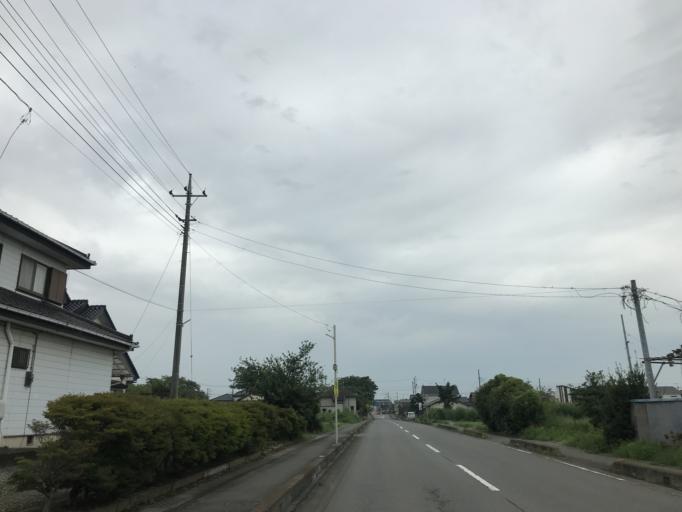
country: JP
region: Ibaraki
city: Sakai
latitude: 36.1111
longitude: 139.7895
